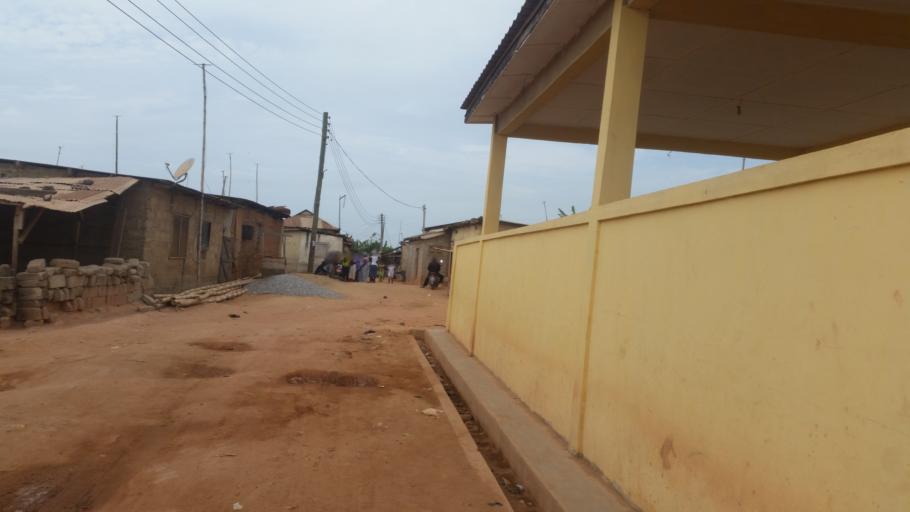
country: GH
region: Central
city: Cape Coast
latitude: 5.1244
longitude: -1.3025
